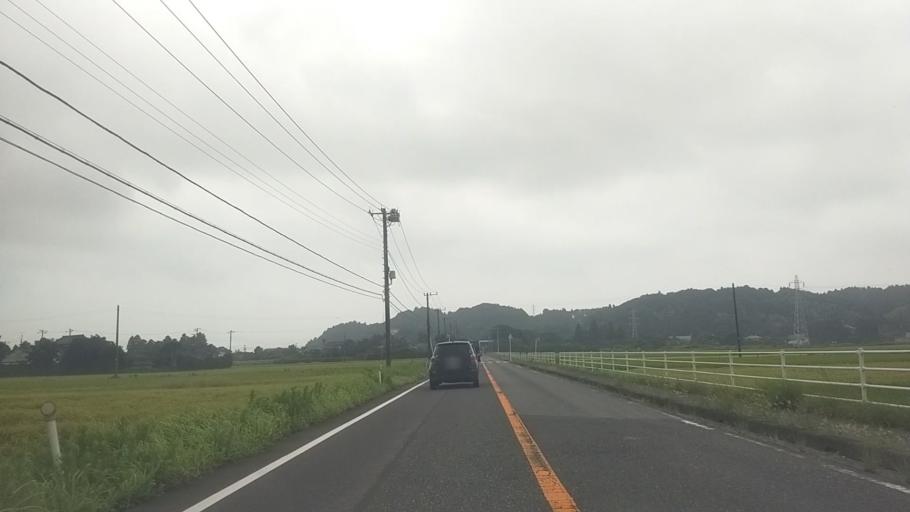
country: JP
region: Chiba
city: Ohara
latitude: 35.2629
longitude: 140.3736
